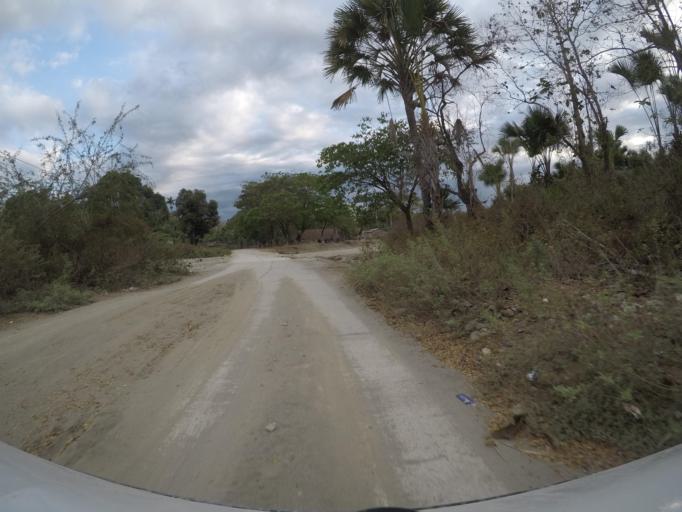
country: TL
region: Bobonaro
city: Maliana
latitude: -8.8733
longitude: 125.2123
